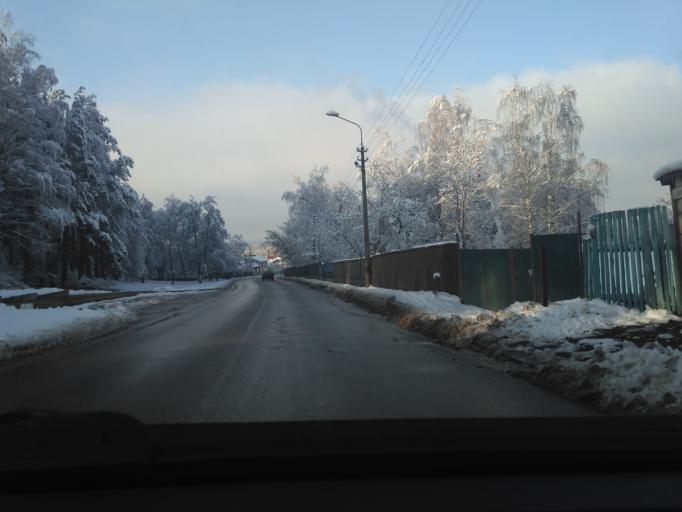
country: BY
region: Minsk
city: Horad Barysaw
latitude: 54.2333
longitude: 28.4997
